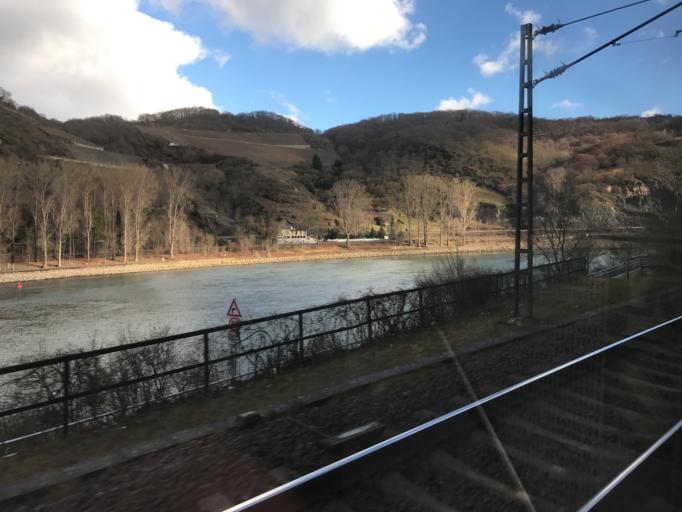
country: DE
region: Rheinland-Pfalz
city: Sankt Goarshausen
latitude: 50.1357
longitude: 7.7321
